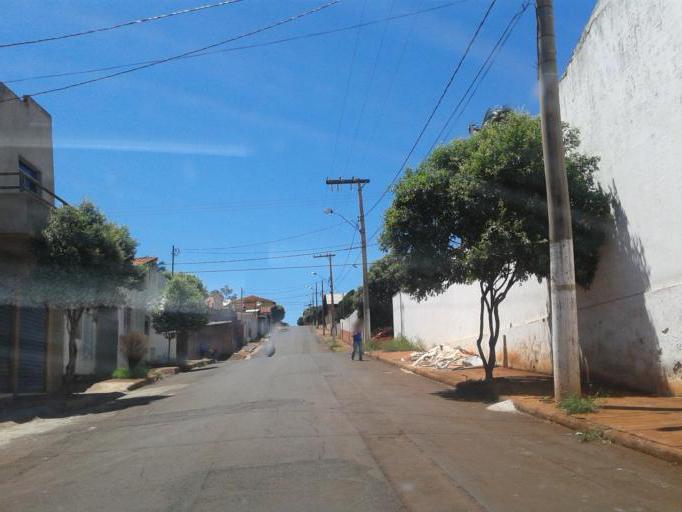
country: BR
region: Minas Gerais
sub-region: Capinopolis
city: Capinopolis
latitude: -18.6805
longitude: -49.5710
